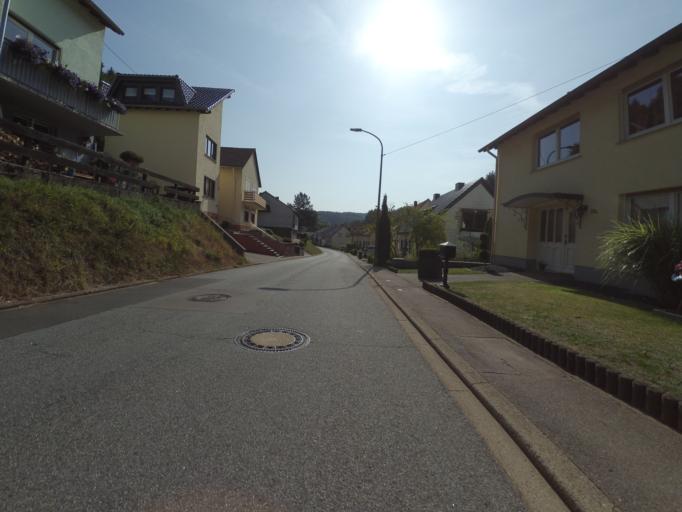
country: DE
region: Rheinland-Pfalz
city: Trassem
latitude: 49.5763
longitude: 6.5160
